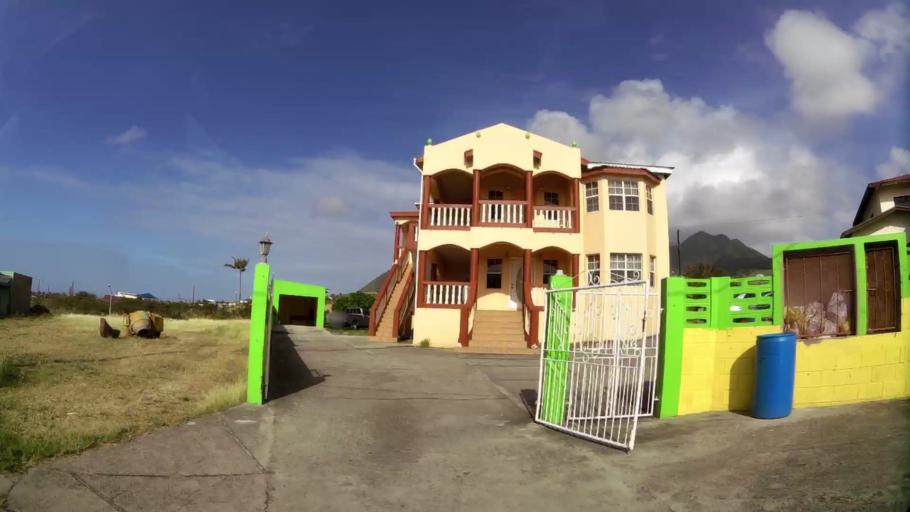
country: KN
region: Saint George Basseterre
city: Basseterre
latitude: 17.2971
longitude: -62.7416
